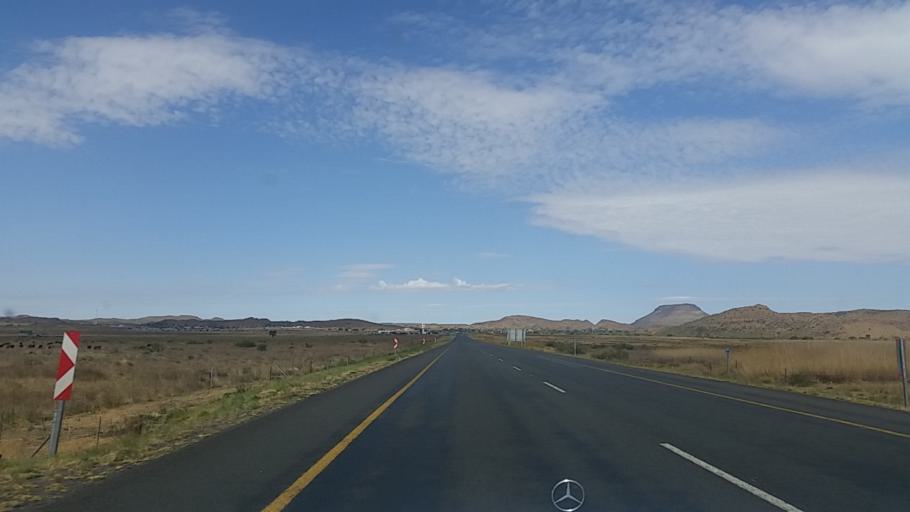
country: ZA
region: Northern Cape
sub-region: Pixley ka Seme District Municipality
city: Colesberg
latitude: -30.6955
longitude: 25.1364
